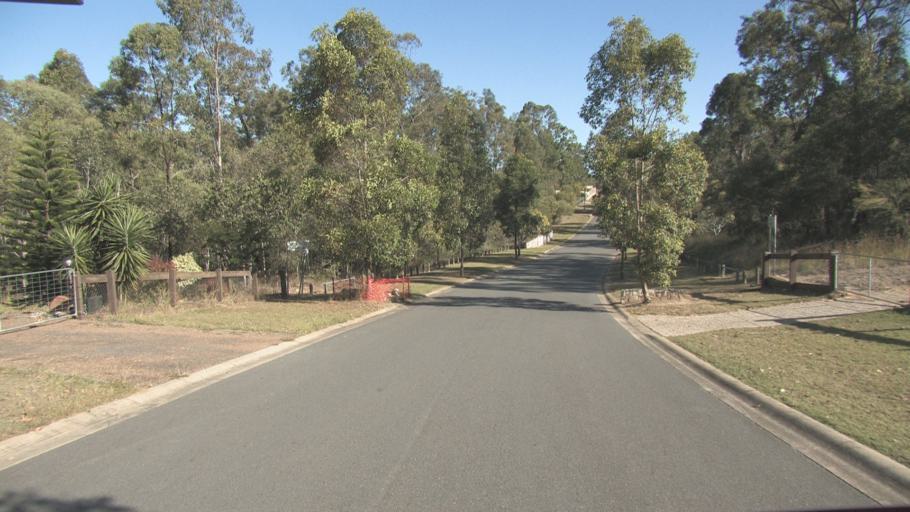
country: AU
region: Queensland
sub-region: Ipswich
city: Springfield Lakes
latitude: -27.7245
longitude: 152.9243
